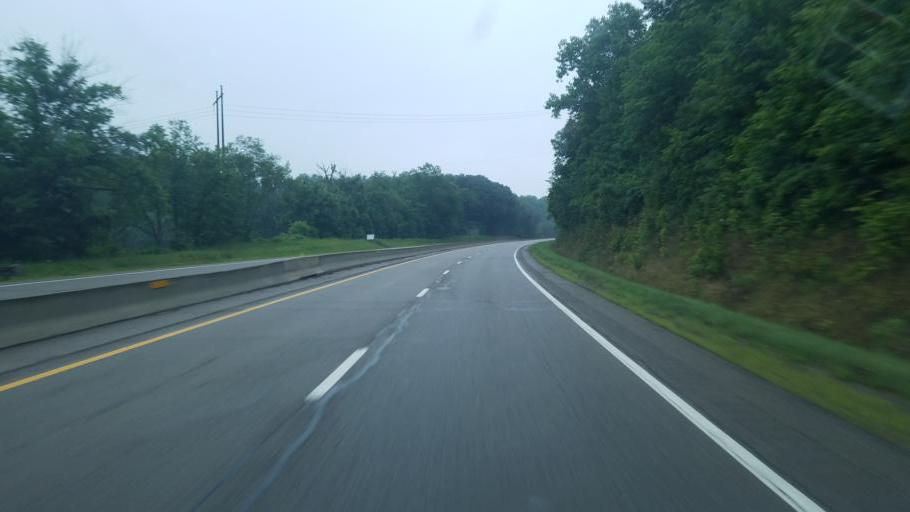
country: US
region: Ohio
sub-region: Tuscarawas County
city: Newcomerstown
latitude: 40.2835
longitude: -81.6337
